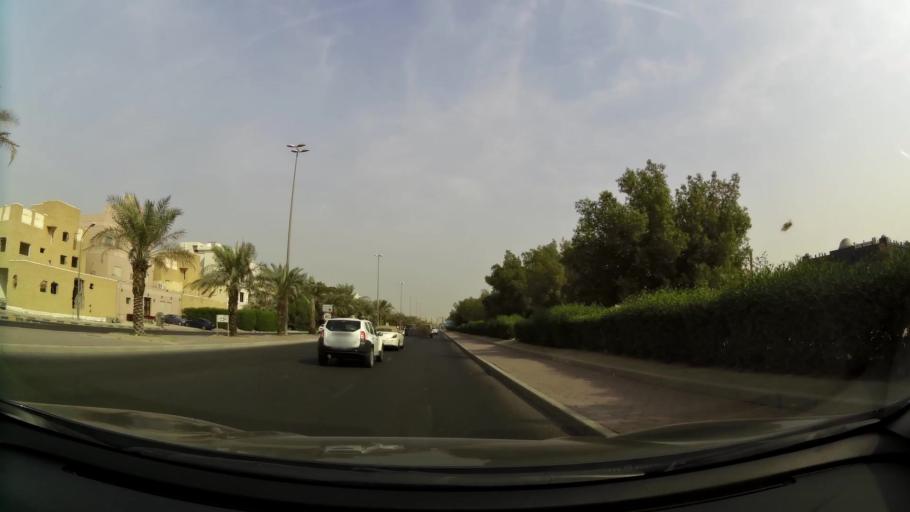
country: KW
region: Al Asimah
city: Ar Rabiyah
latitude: 29.2801
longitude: 47.9302
